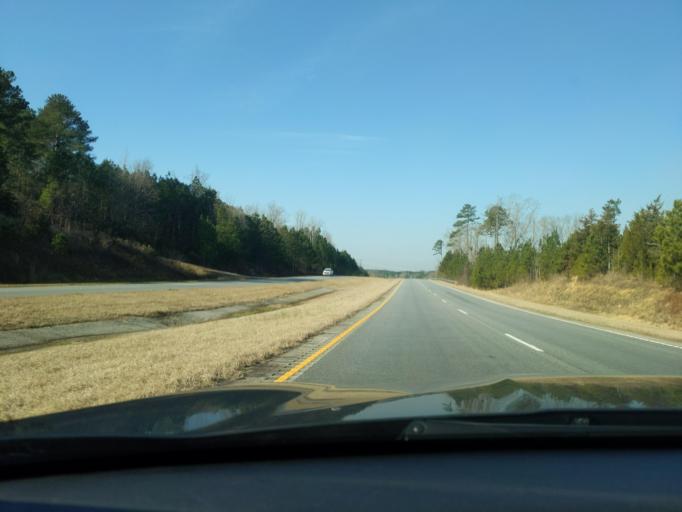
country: US
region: South Carolina
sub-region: Abbeville County
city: Calhoun Falls
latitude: 34.1110
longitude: -82.5015
